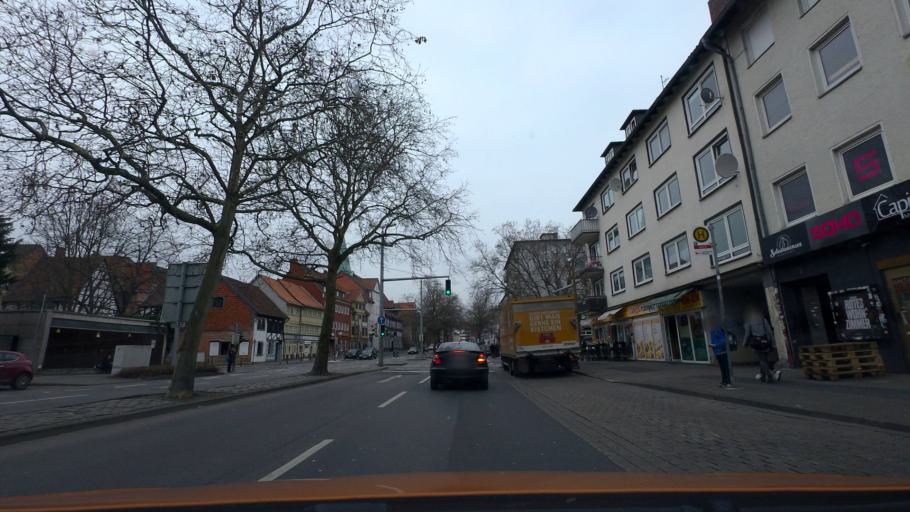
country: DE
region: Lower Saxony
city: Braunschweig
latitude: 52.2595
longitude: 10.5161
